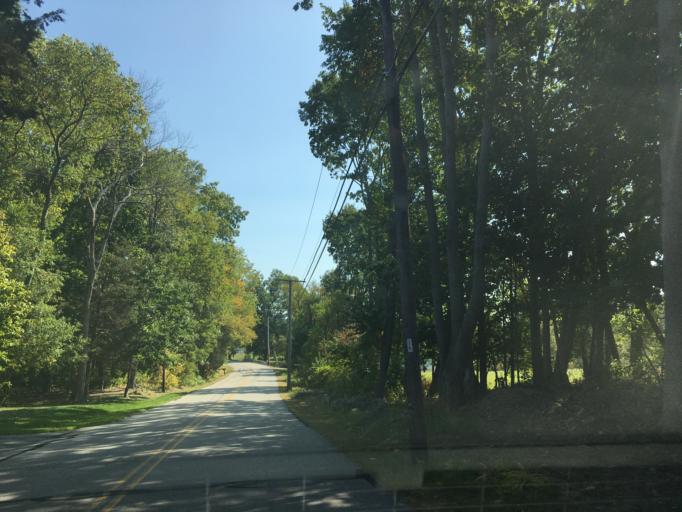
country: US
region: New Hampshire
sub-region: Rockingham County
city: Exeter
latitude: 43.0028
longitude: -70.9148
